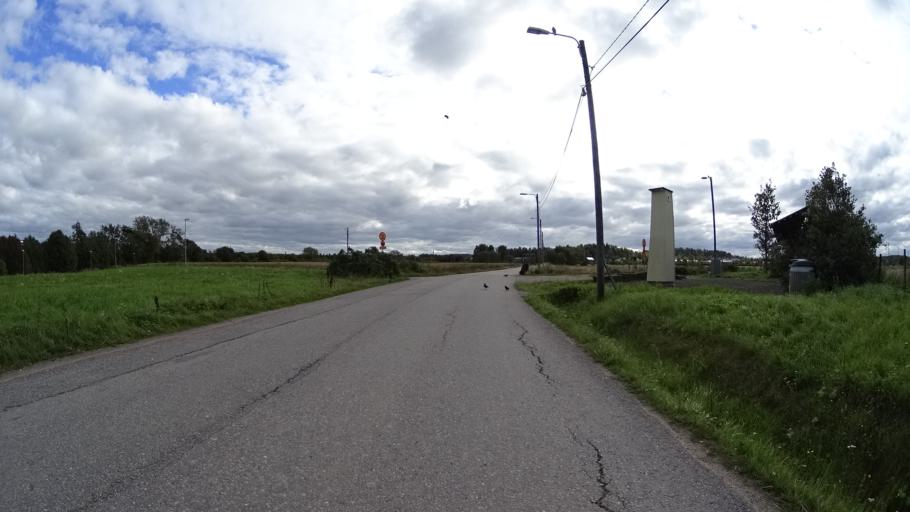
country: FI
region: Uusimaa
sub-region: Helsinki
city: Vantaa
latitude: 60.2709
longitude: 24.9562
